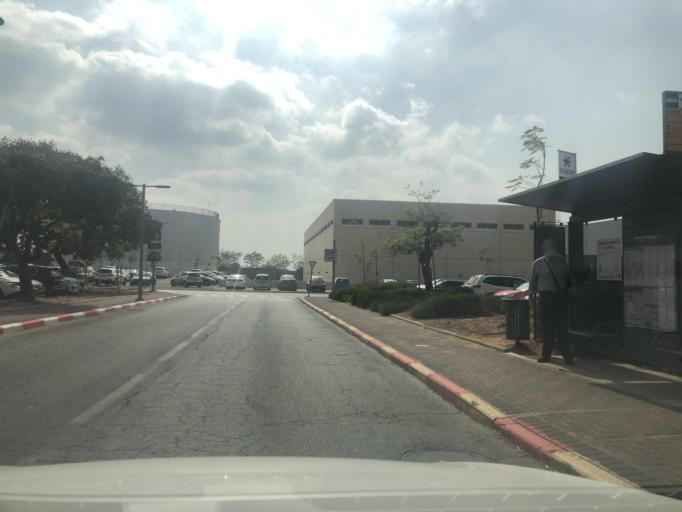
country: IL
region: Tel Aviv
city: Or Yehuda
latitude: 32.0448
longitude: 34.8458
